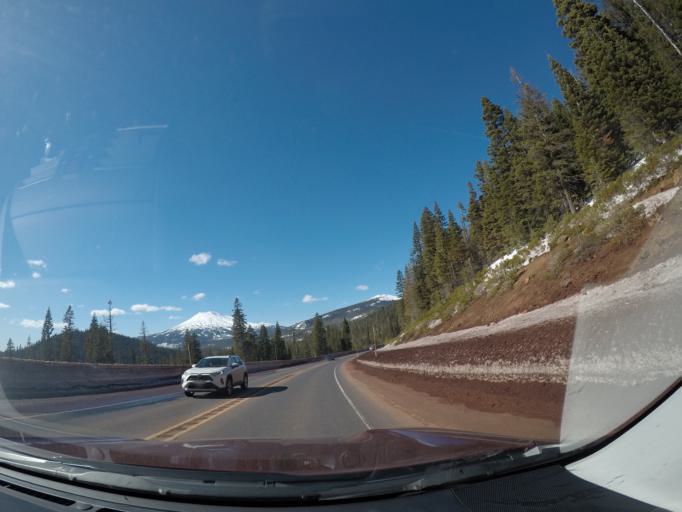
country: US
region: Oregon
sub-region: Deschutes County
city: Sunriver
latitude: 43.9803
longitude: -121.5876
